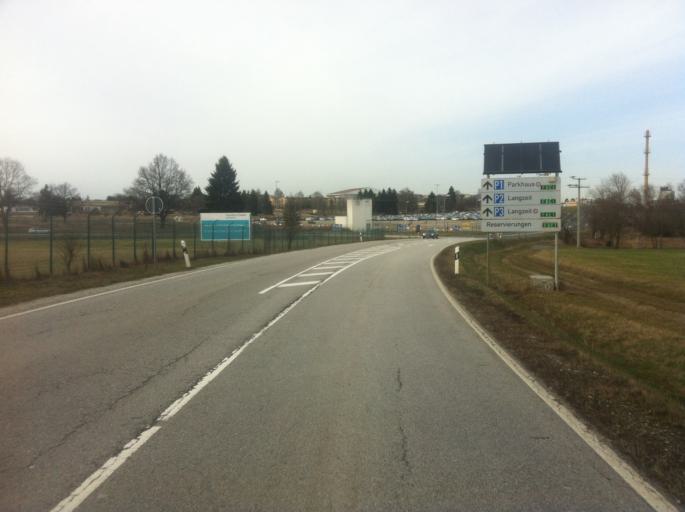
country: DE
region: Rheinland-Pfalz
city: Lautzenhausen
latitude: 49.9355
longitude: 7.2678
